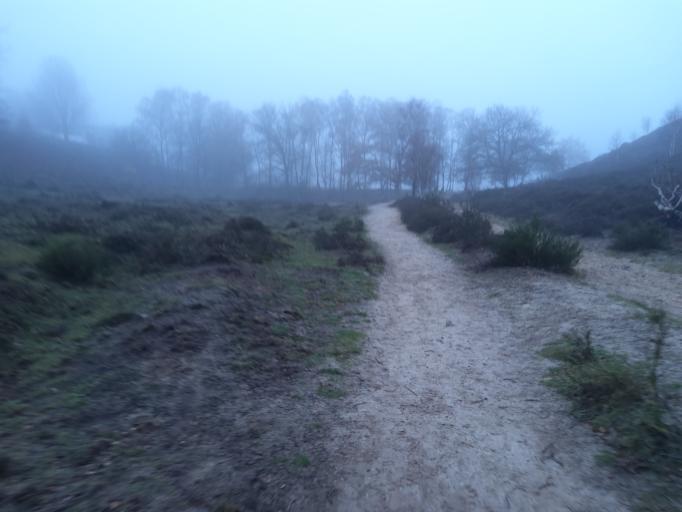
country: NL
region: Gelderland
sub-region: Gemeente Rheden
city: Rheden
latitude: 52.0242
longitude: 6.0167
